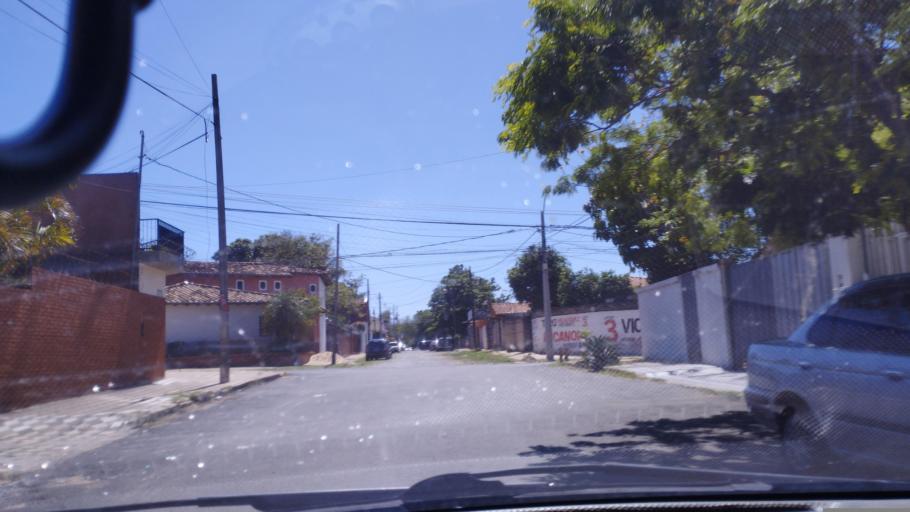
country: PY
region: Asuncion
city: Asuncion
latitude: -25.2969
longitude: -57.6638
